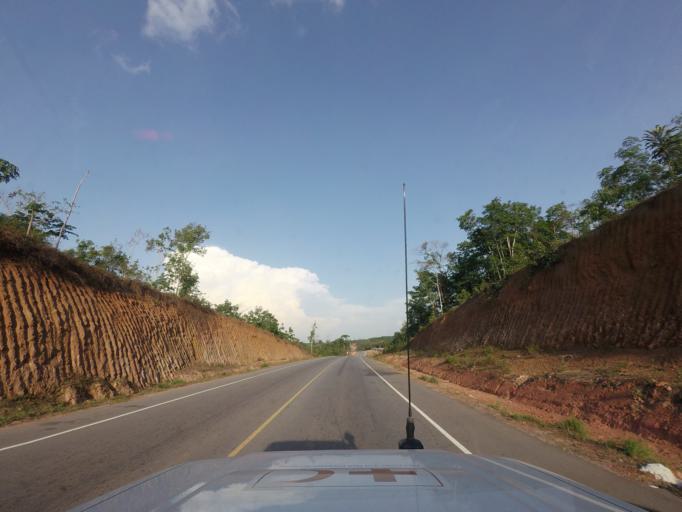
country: LR
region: Bong
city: Gbarnga
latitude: 7.0052
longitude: -9.3193
